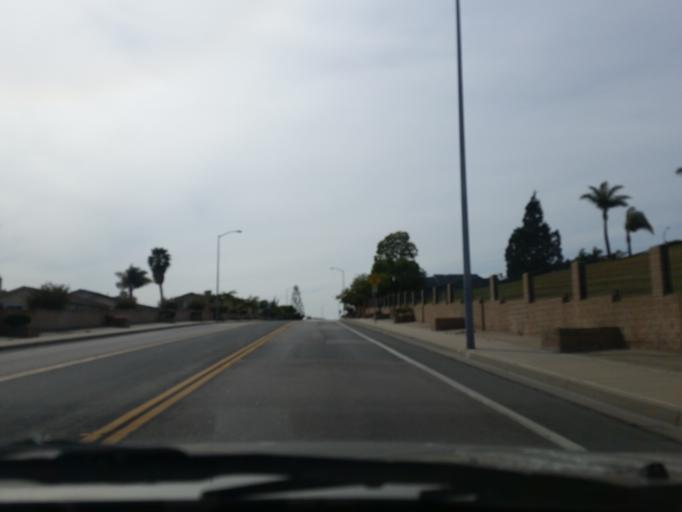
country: US
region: California
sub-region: San Luis Obispo County
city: Grover Beach
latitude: 35.1348
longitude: -120.6083
